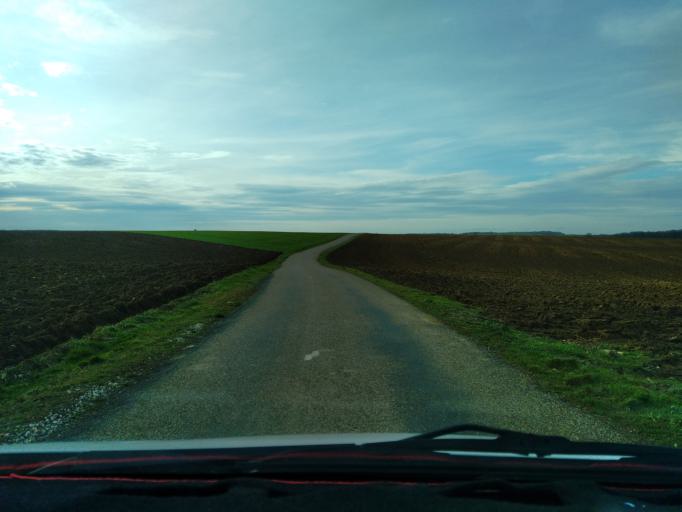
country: FR
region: Franche-Comte
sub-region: Departement de la Haute-Saone
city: Marnay
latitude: 47.3633
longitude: 5.7120
